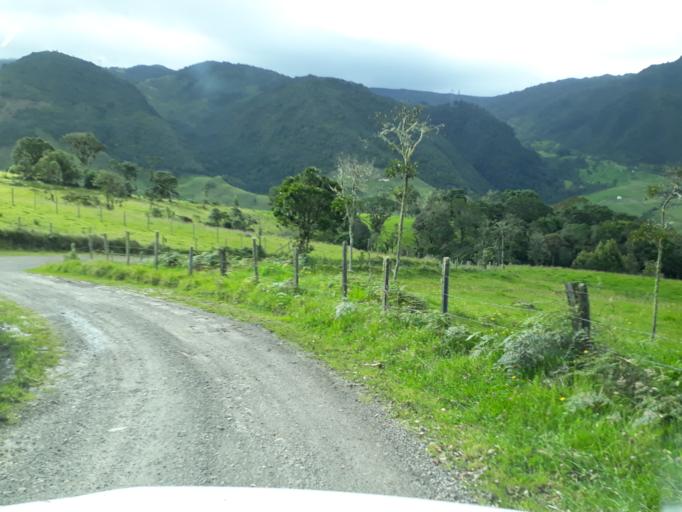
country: CO
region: Cundinamarca
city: Junin
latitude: 4.8152
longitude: -73.7731
